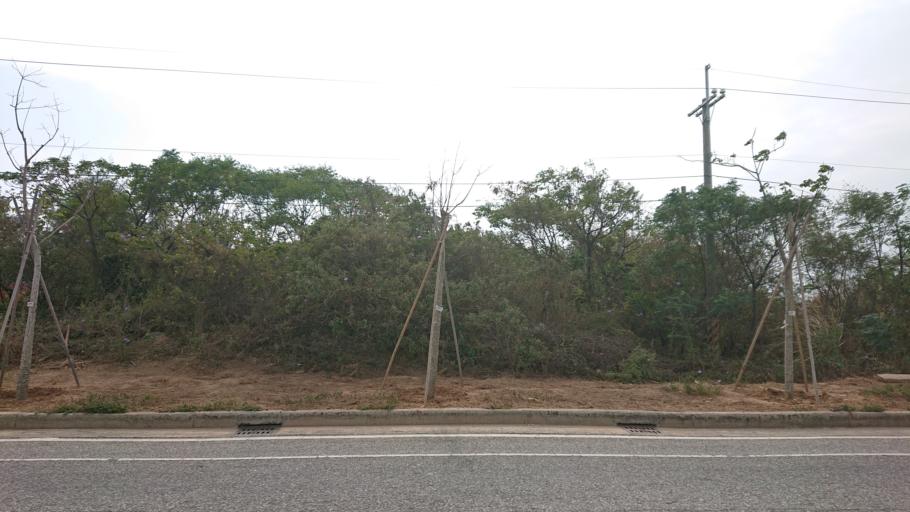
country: TW
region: Fukien
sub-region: Kinmen
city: Jincheng
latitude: 24.4562
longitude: 118.3772
